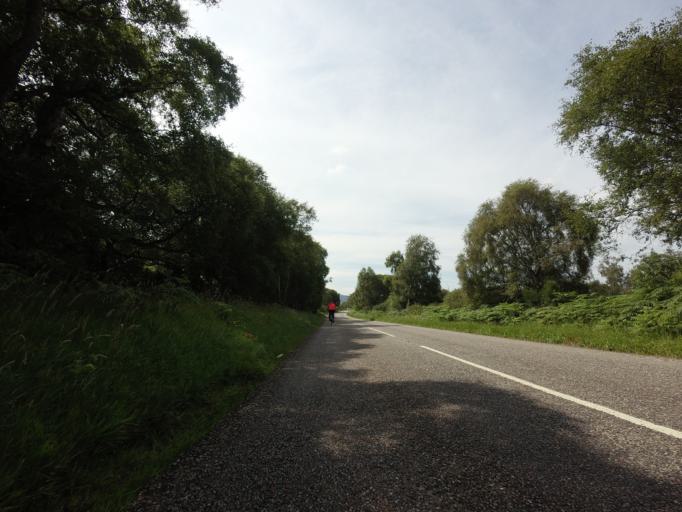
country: GB
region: Scotland
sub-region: Highland
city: Alness
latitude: 57.8571
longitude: -4.2455
